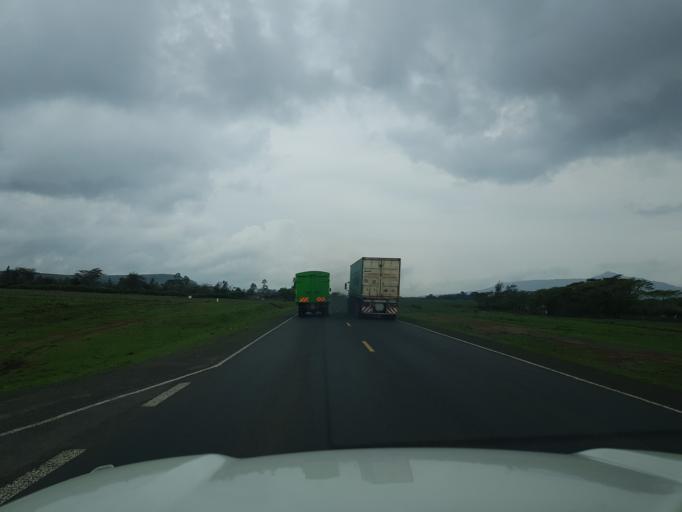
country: KE
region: Nakuru
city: Naivasha
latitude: -0.8155
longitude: 36.4673
